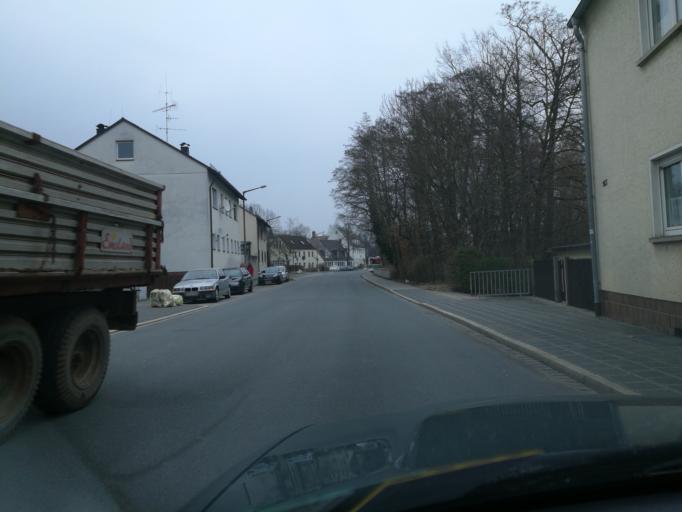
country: DE
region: Bavaria
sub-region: Regierungsbezirk Mittelfranken
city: Furth
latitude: 49.4912
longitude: 10.9536
